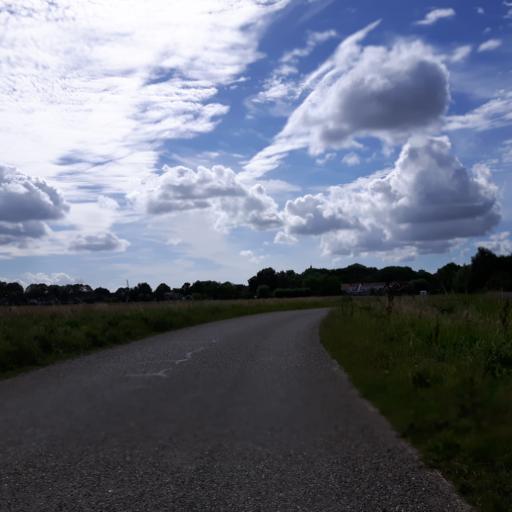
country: NL
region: Zeeland
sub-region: Gemeente Goes
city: Goes
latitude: 51.4998
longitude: 3.9295
